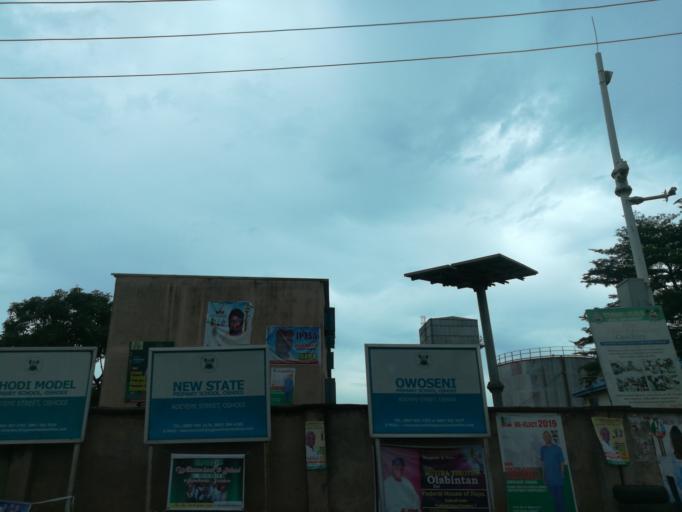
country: NG
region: Lagos
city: Oshodi
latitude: 6.5611
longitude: 3.3431
